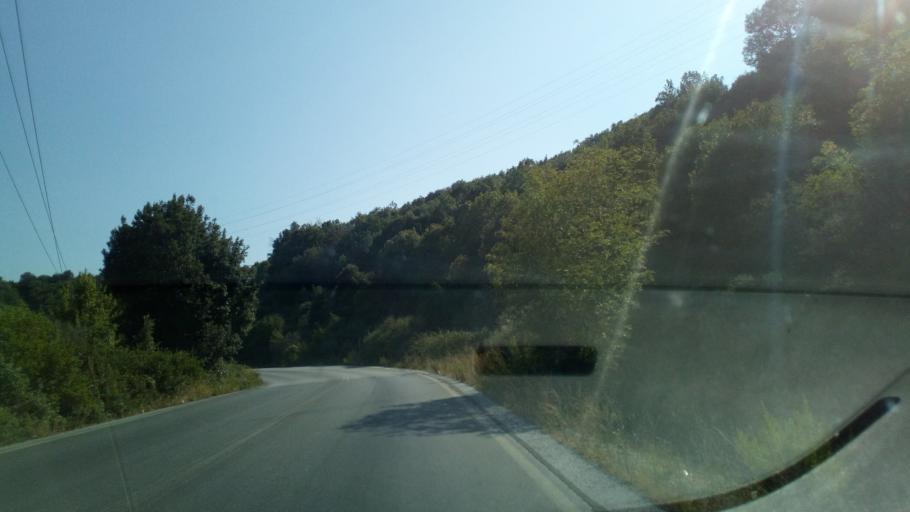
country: GR
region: Central Macedonia
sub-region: Nomos Thessalonikis
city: Stavros
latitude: 40.6541
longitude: 23.7400
